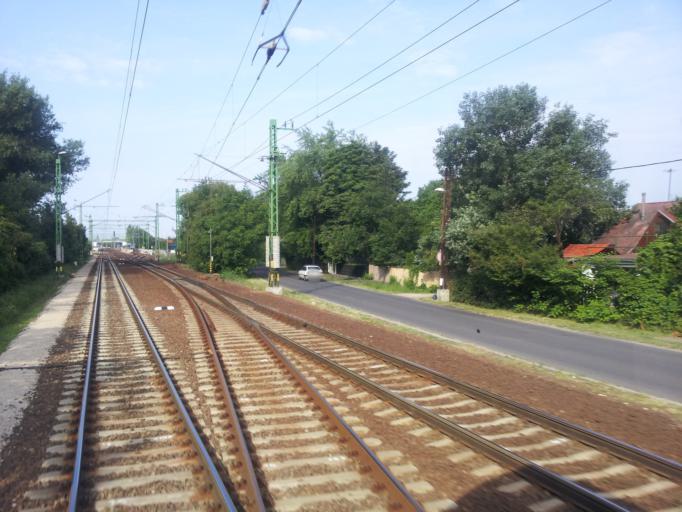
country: HU
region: Fejer
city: Gardony
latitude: 47.2083
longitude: 18.6287
